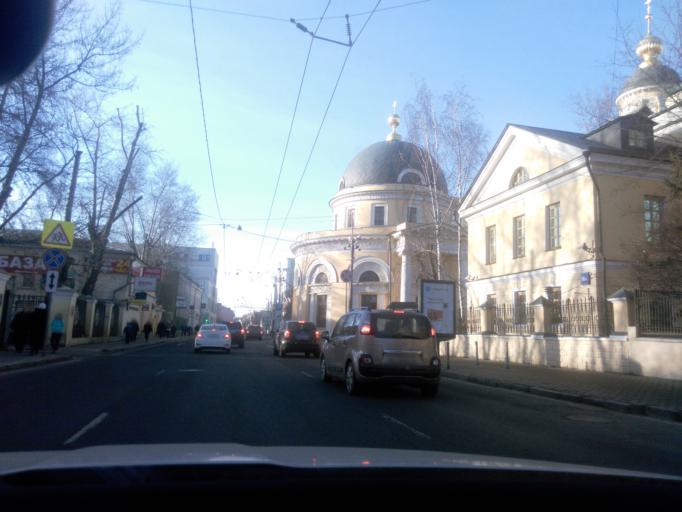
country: RU
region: Moscow
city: Zamoskvorech'ye
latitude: 55.7421
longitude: 37.6251
